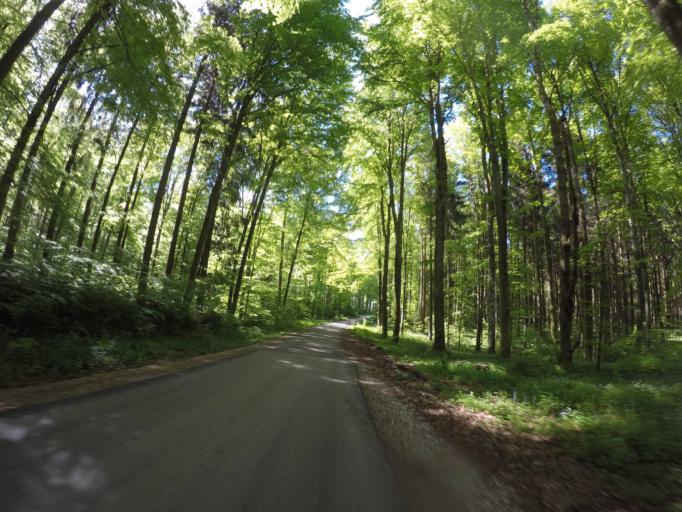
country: DE
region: Baden-Wuerttemberg
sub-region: Tuebingen Region
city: Laichingen
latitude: 48.4439
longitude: 9.7080
